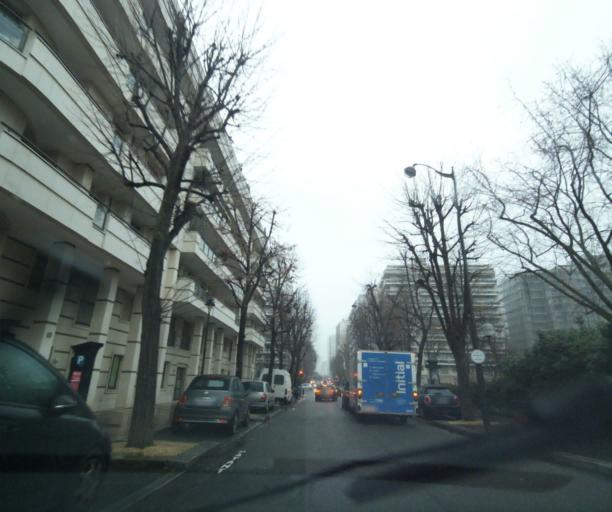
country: FR
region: Ile-de-France
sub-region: Departement des Hauts-de-Seine
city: Levallois-Perret
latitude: 48.8895
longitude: 2.2916
